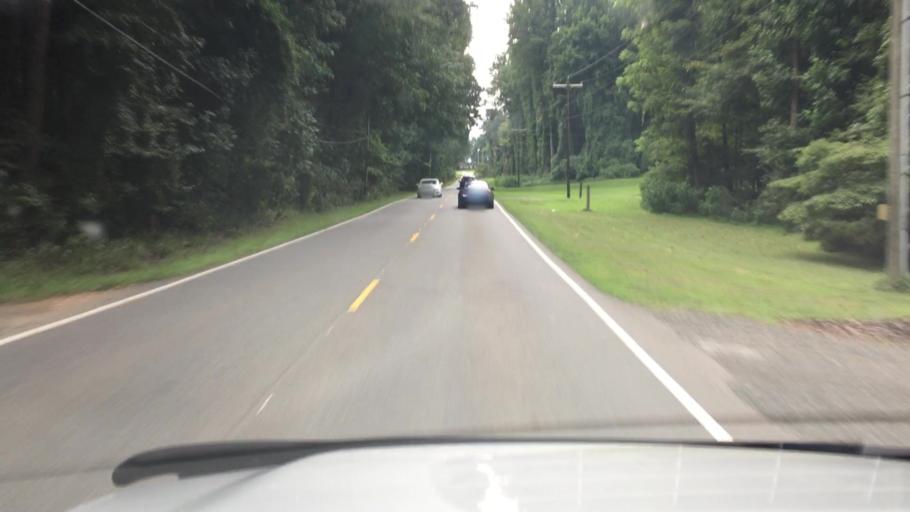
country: US
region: North Carolina
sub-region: Mecklenburg County
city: Huntersville
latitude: 35.3572
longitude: -80.8937
